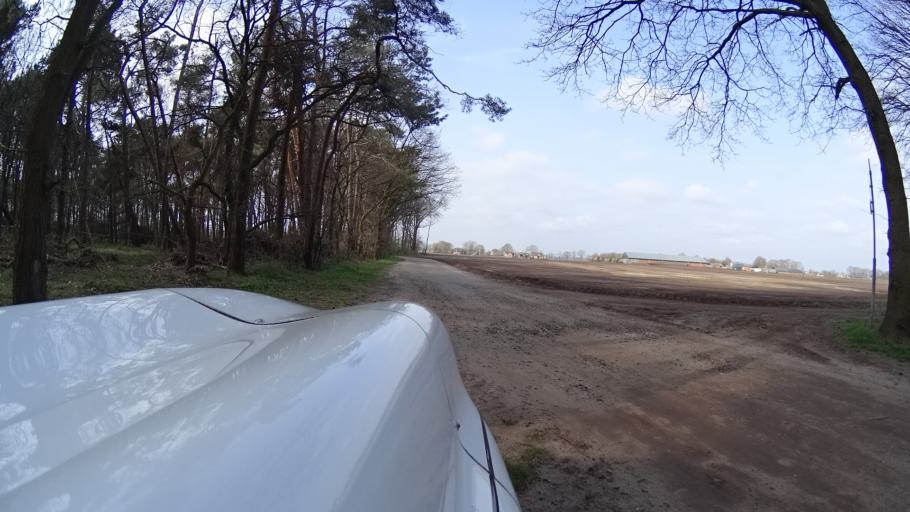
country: NL
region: North Brabant
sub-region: Gemeente Boekel
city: Boekel
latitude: 51.5815
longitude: 5.6981
